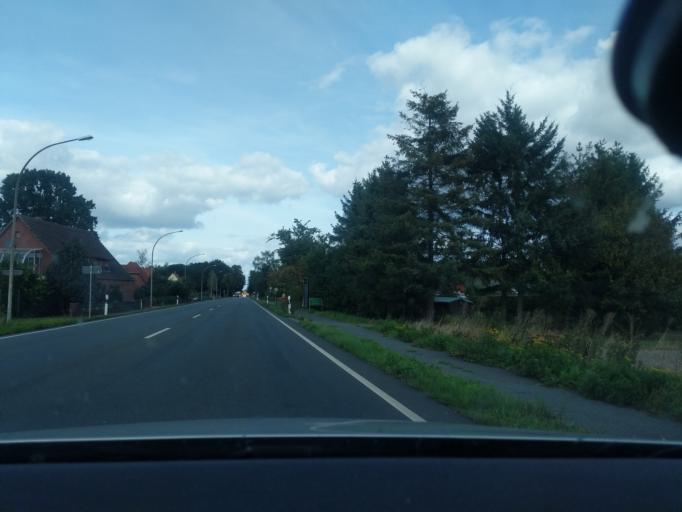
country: DE
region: Lower Saxony
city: Dorverden
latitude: 52.8336
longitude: 9.2125
